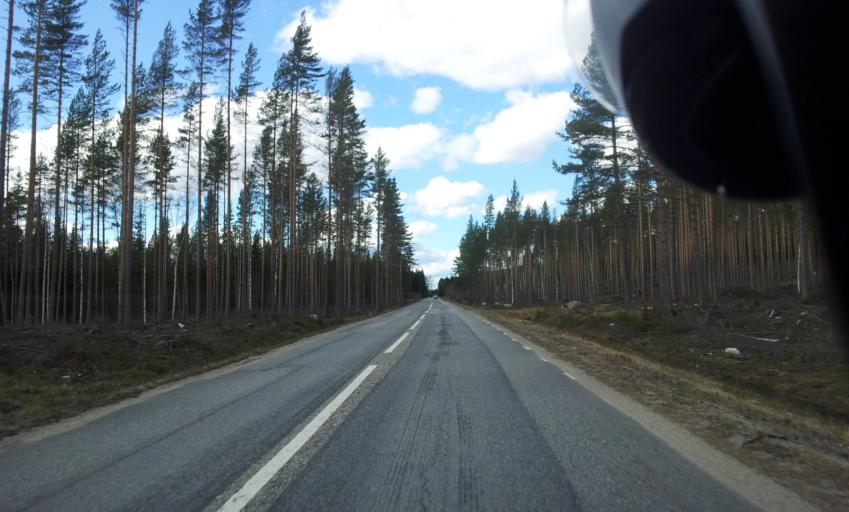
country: SE
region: Gaevleborg
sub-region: Ovanakers Kommun
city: Edsbyn
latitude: 61.2887
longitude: 15.9048
